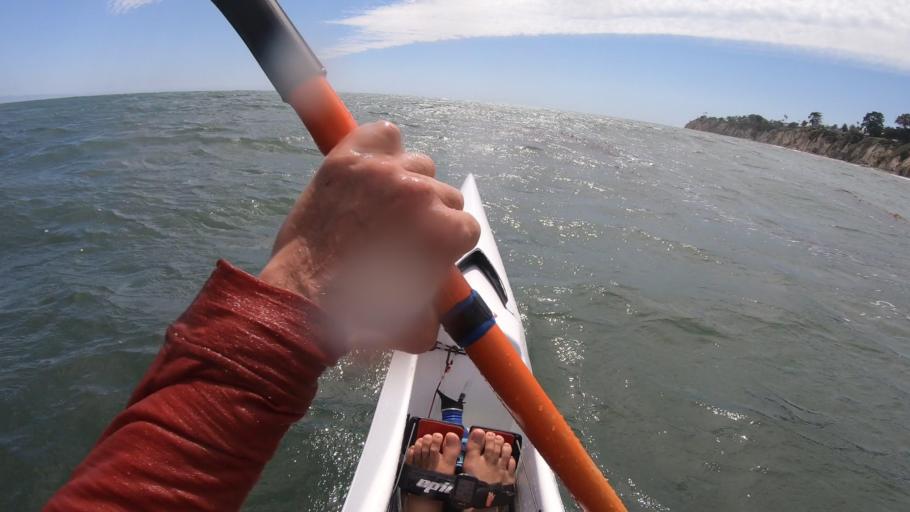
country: US
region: California
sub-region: Santa Barbara County
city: Santa Barbara
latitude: 34.3944
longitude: -119.7052
